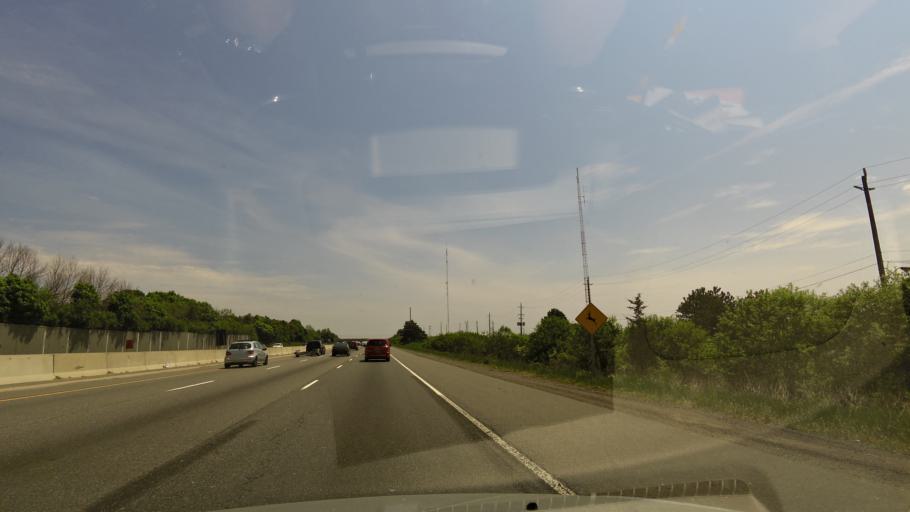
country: CA
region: Ontario
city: Ajax
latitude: 43.8666
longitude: -78.9473
